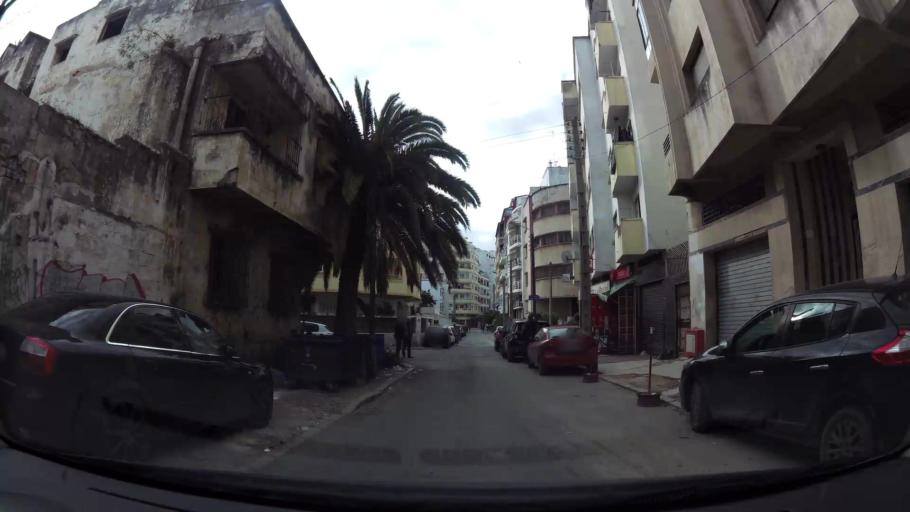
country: MA
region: Tanger-Tetouan
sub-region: Tanger-Assilah
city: Tangier
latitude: 35.7748
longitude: -5.8128
